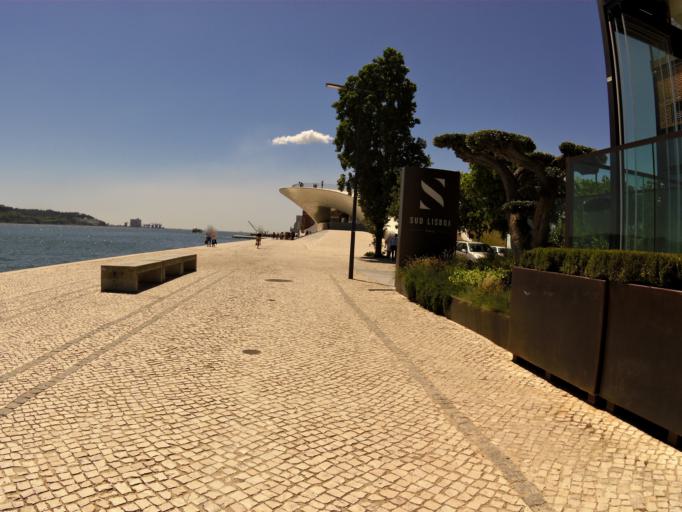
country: PT
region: Setubal
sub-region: Almada
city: Caparica
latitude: 38.6961
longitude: -9.1920
